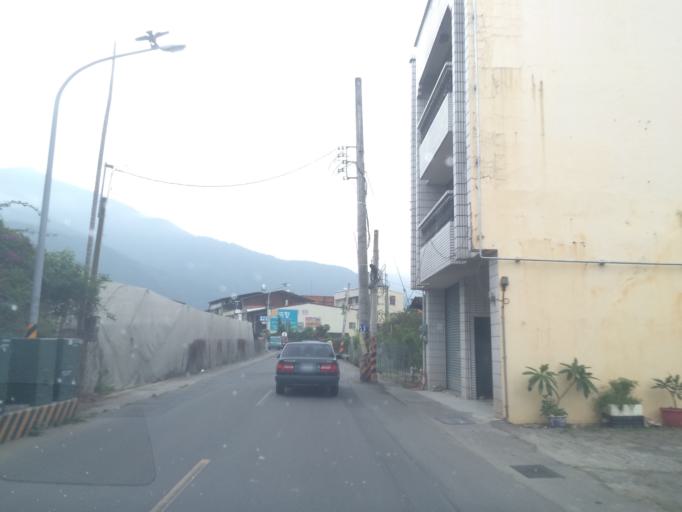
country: TW
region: Taiwan
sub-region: Nantou
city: Puli
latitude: 23.9556
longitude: 120.9769
